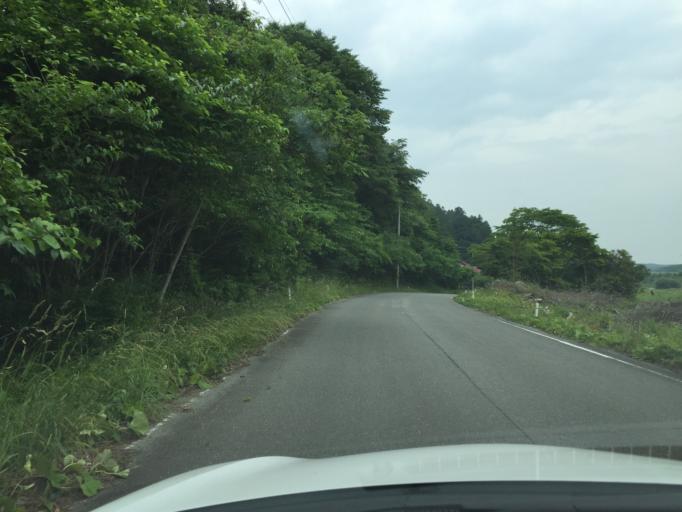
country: JP
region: Fukushima
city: Iwaki
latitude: 37.1747
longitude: 140.7135
